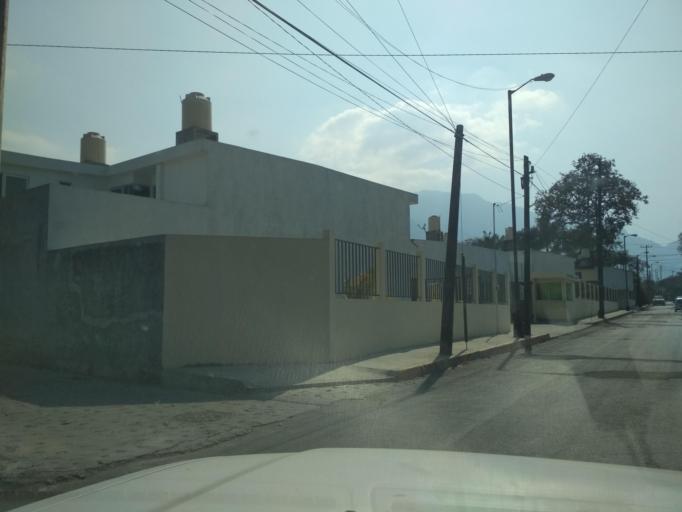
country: MX
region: Veracruz
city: Jalapilla
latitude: 18.8389
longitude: -97.0837
